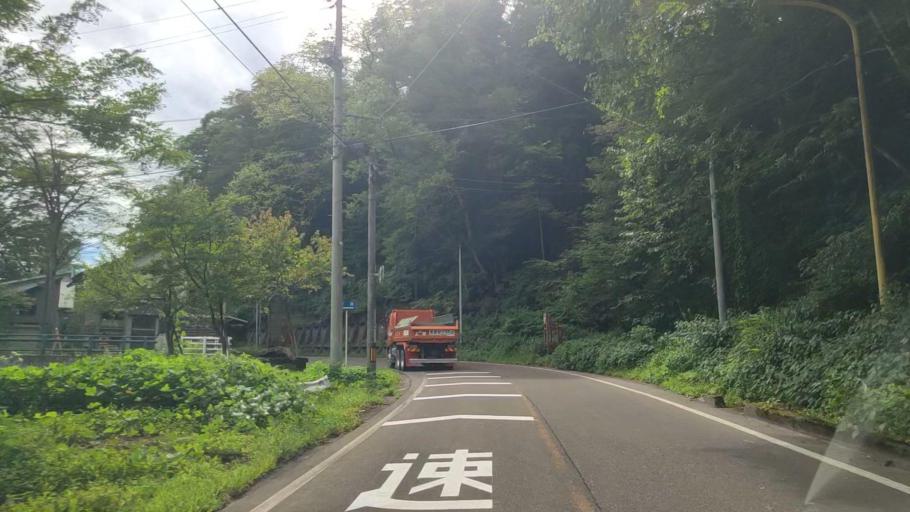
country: JP
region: Niigata
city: Arai
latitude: 36.9556
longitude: 138.2720
